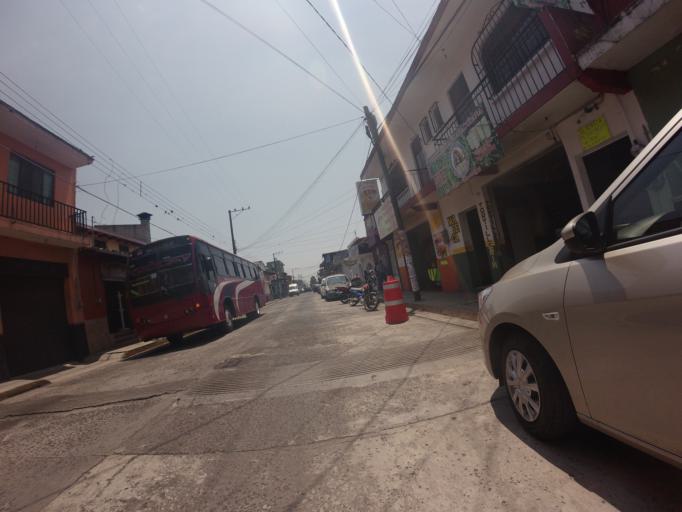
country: MX
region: Veracruz
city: Coatepec
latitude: 19.4525
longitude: -96.9609
